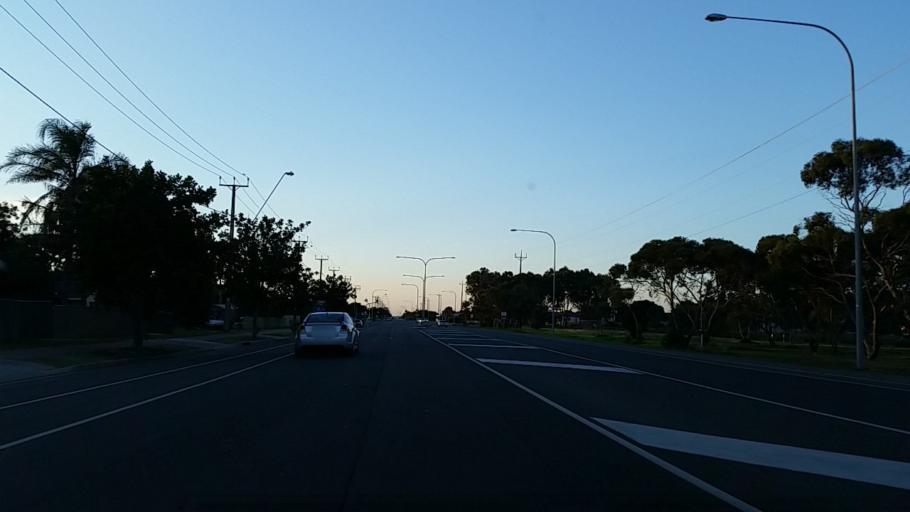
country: AU
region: South Australia
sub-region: Onkaparinga
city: Seaford
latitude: -35.1832
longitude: 138.4769
